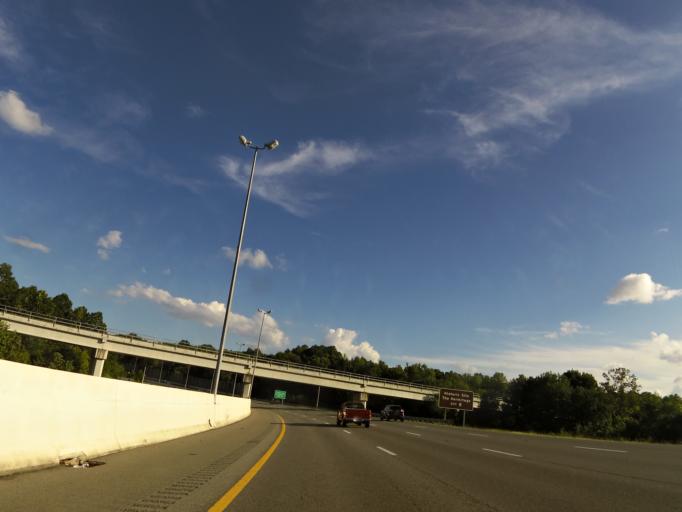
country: US
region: Tennessee
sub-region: Davidson County
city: Lakewood
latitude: 36.1800
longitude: -86.6958
